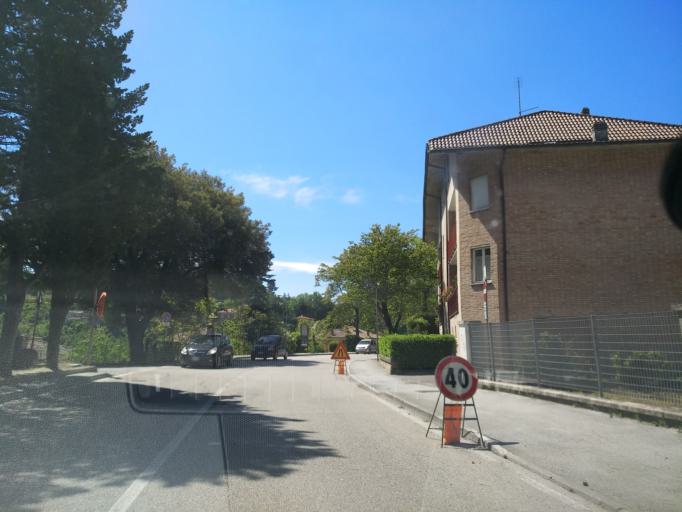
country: IT
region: The Marches
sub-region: Provincia di Pesaro e Urbino
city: Urbino
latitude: 43.7318
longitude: 12.6320
